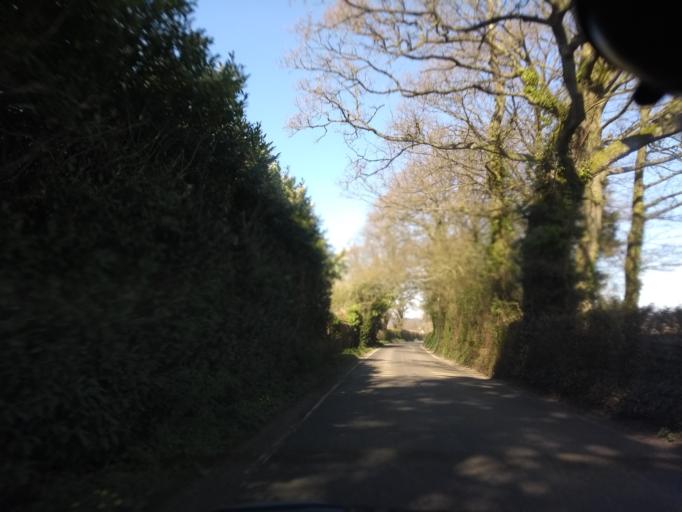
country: GB
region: England
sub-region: Somerset
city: Taunton
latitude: 51.0370
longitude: -3.1101
